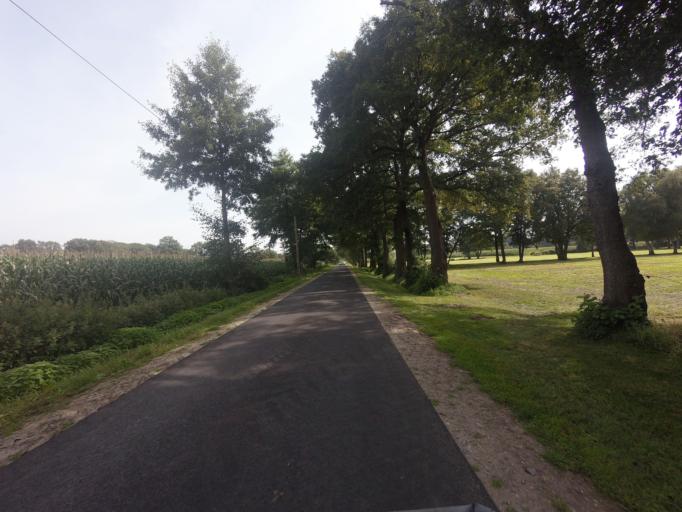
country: DE
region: Lower Saxony
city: Wielen
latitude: 52.5308
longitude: 6.7608
